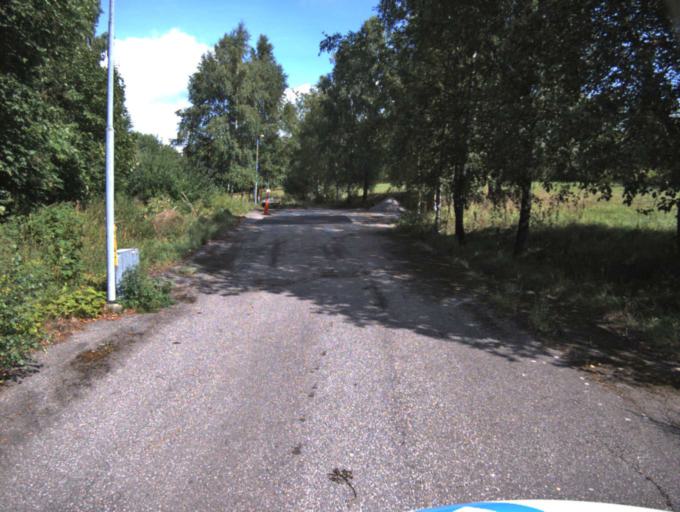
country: SE
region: Vaestra Goetaland
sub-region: Ulricehamns Kommun
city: Ulricehamn
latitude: 57.7005
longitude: 13.5002
